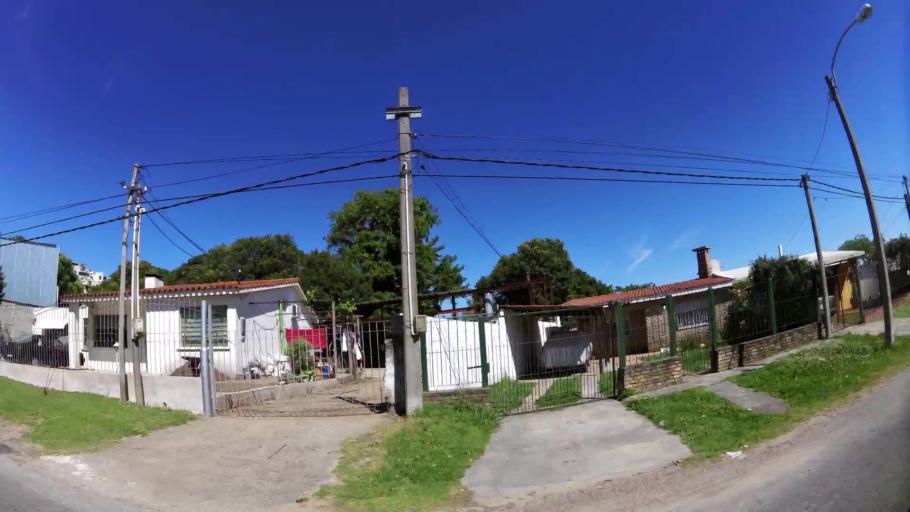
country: UY
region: Montevideo
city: Montevideo
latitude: -34.8670
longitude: -56.1282
